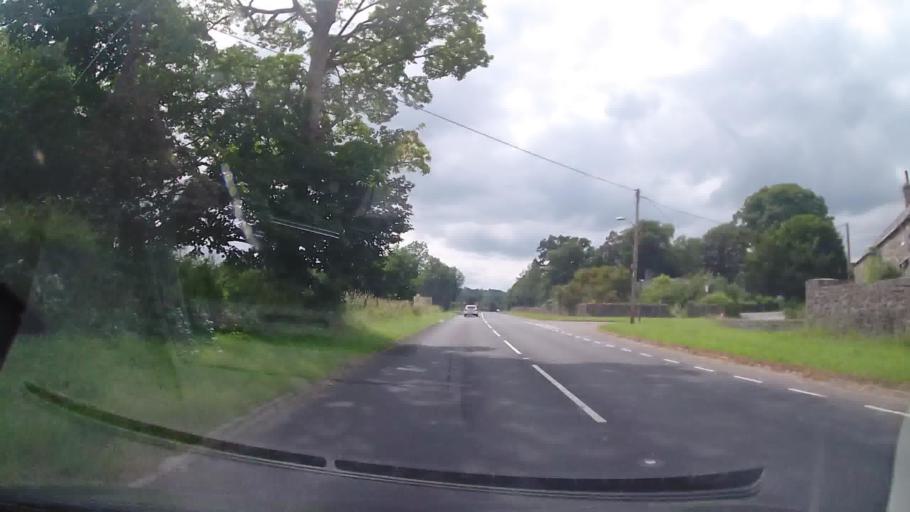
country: GB
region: Wales
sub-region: Gwynedd
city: Bala
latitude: 52.9163
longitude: -3.5790
